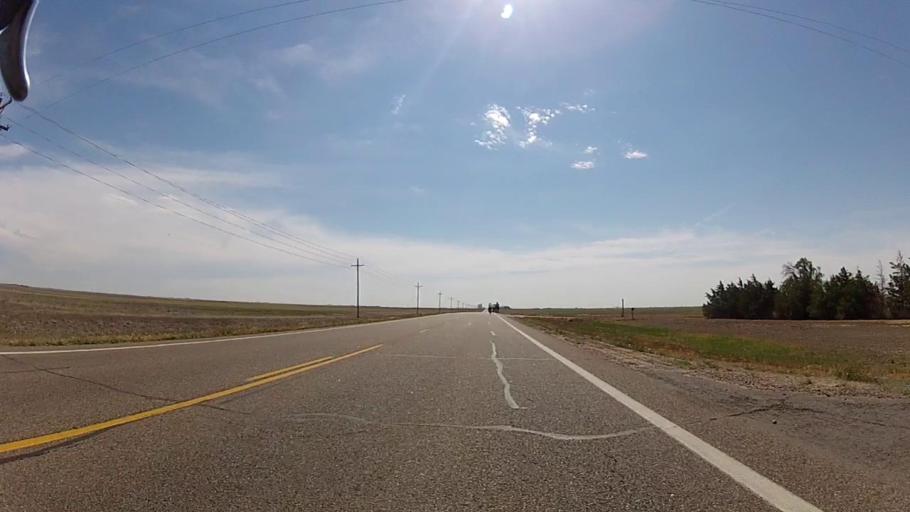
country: US
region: Kansas
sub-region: Grant County
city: Ulysses
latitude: 37.5618
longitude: -101.2848
